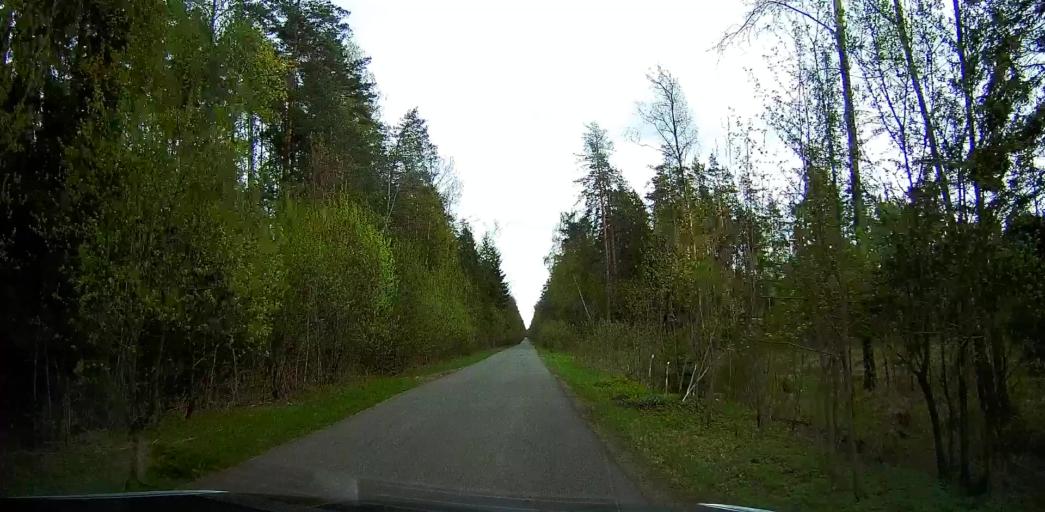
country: RU
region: Moskovskaya
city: Malyshevo
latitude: 55.5489
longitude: 38.3606
